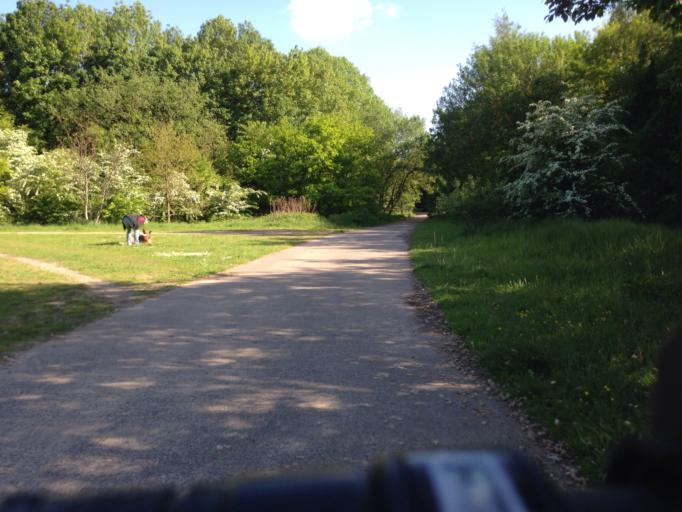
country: DE
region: Schleswig-Holstein
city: Stapelfeld
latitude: 53.6106
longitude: 10.1886
